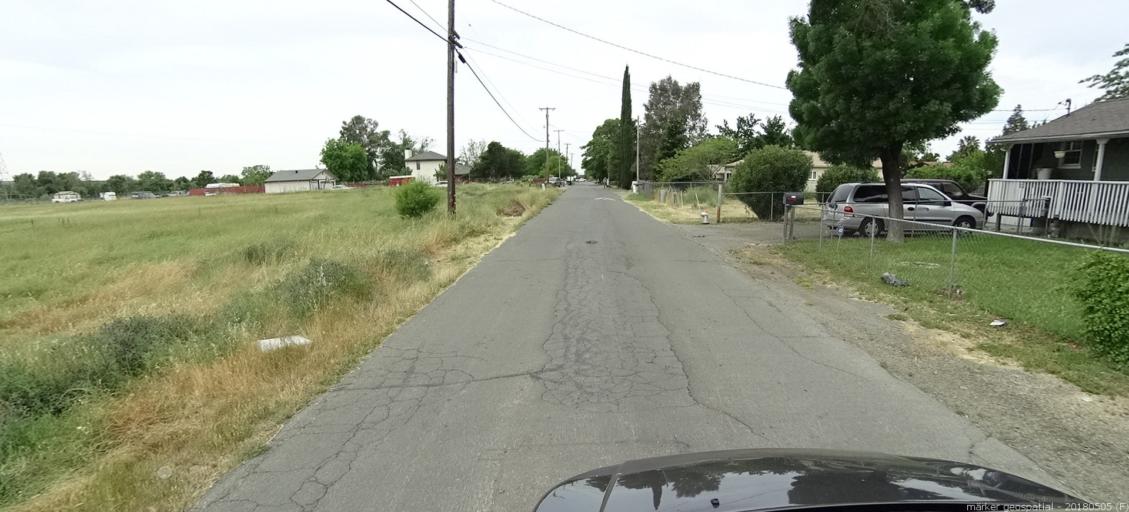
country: US
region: California
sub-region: Sacramento County
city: Rio Linda
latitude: 38.6439
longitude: -121.4444
